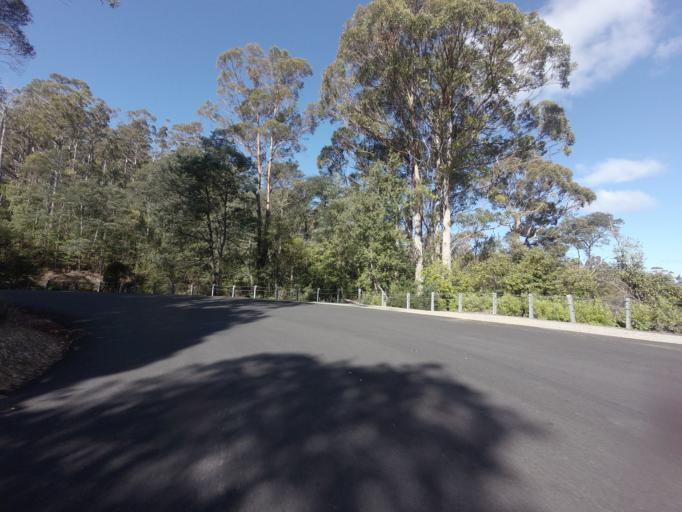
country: AU
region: Tasmania
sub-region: Break O'Day
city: St Helens
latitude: -41.6345
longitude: 148.2424
